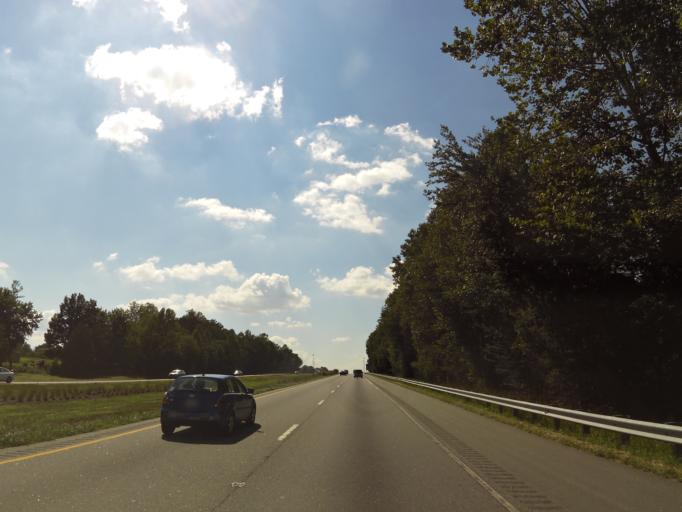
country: US
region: North Carolina
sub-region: Burke County
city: Hildebran
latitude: 35.7057
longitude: -81.4140
